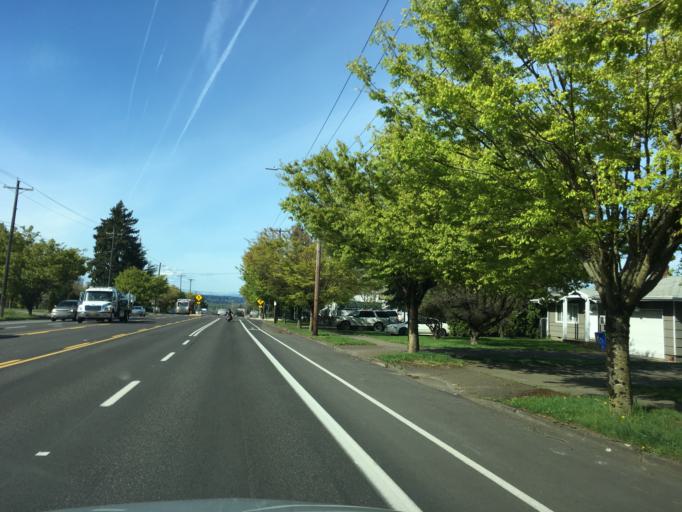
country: US
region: Oregon
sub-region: Multnomah County
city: Lents
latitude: 45.5418
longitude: -122.5374
